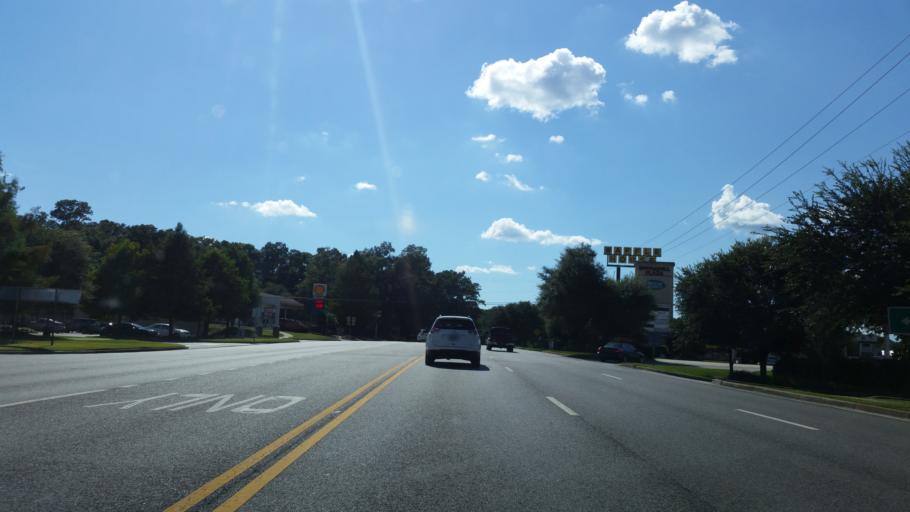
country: US
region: Alabama
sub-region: Mobile County
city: Prichard
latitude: 30.7039
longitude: -88.1247
